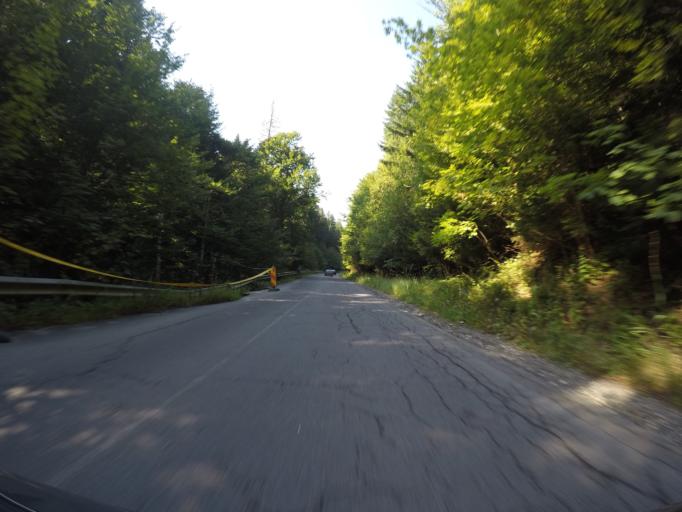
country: RO
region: Brasov
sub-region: Comuna Cristian
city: Cristian
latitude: 45.5976
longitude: 25.5404
